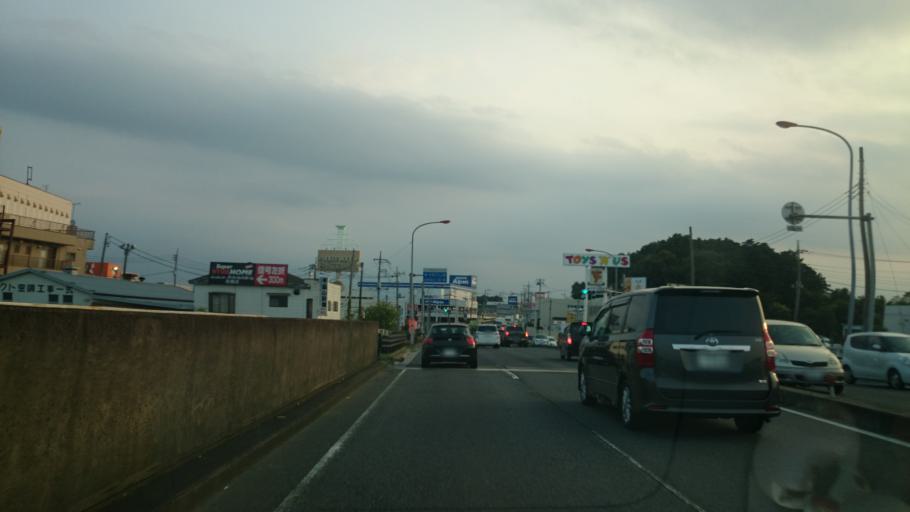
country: JP
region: Saitama
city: Iwatsuki
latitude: 35.9482
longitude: 139.7159
